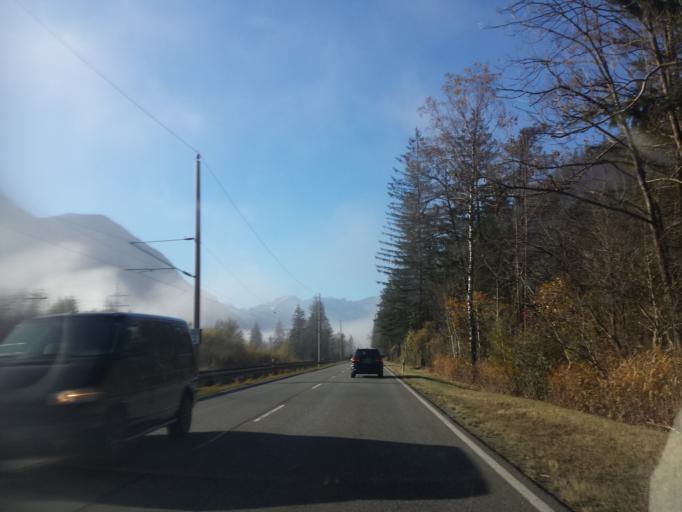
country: DE
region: Bavaria
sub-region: Upper Bavaria
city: Eschenlohe
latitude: 47.5830
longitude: 11.1701
